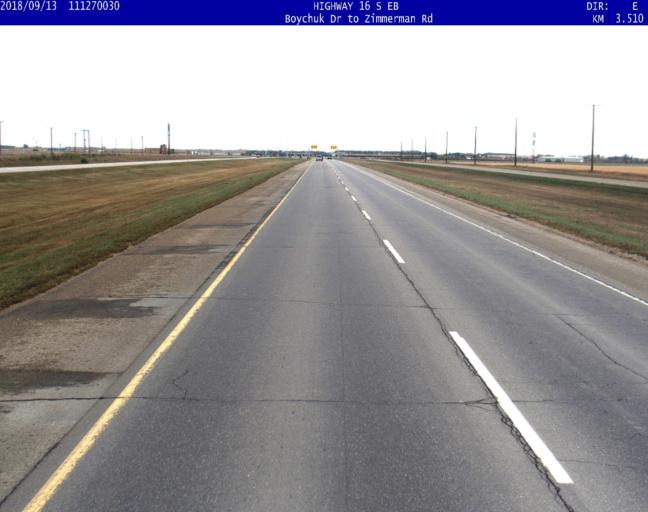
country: CA
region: Saskatchewan
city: Saskatoon
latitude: 52.0859
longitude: -106.5474
